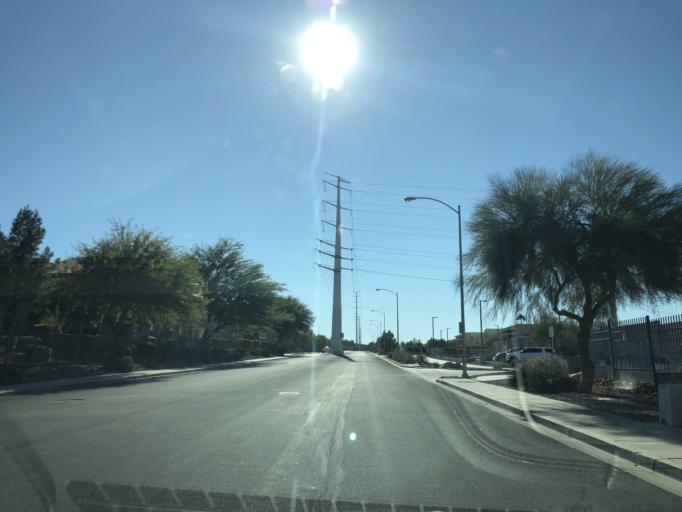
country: US
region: Nevada
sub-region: Clark County
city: Whitney
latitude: 36.0037
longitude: -115.0901
